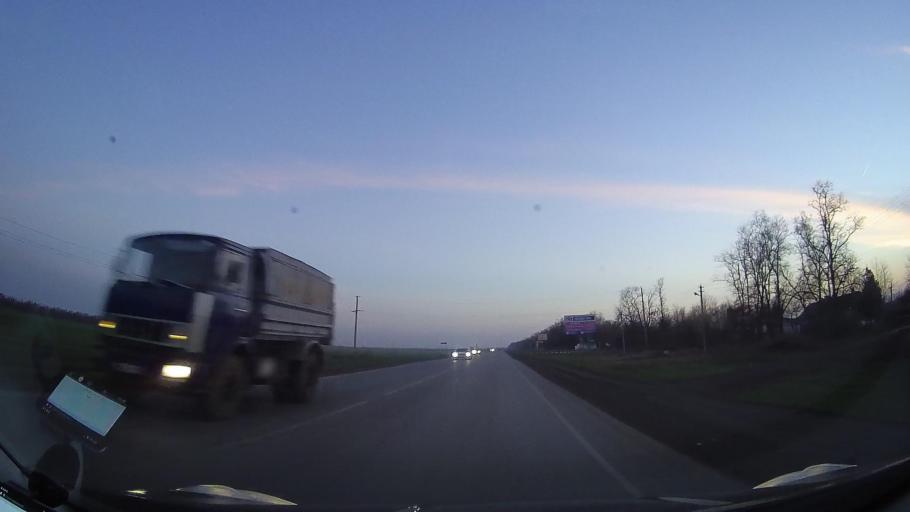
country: RU
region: Rostov
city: Zernograd
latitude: 46.8331
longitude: 40.2994
